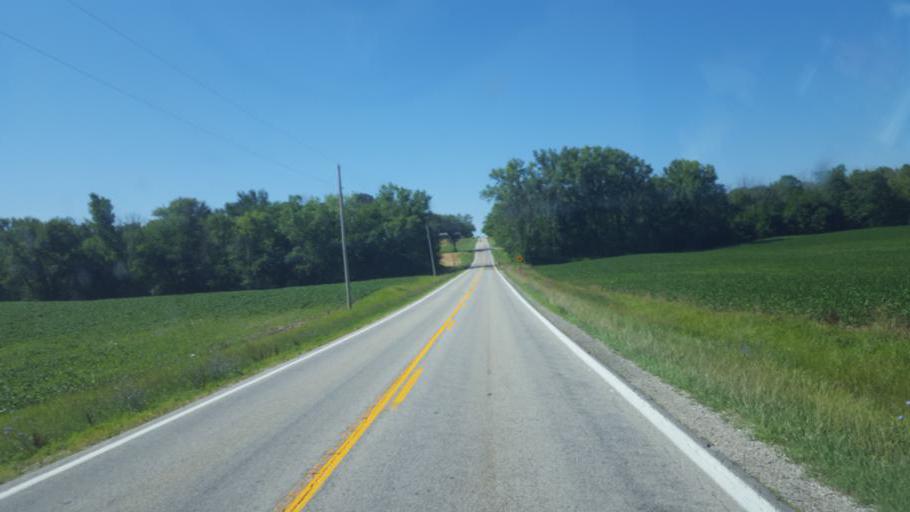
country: US
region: Ohio
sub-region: Knox County
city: Centerburg
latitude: 40.4116
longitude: -82.7046
